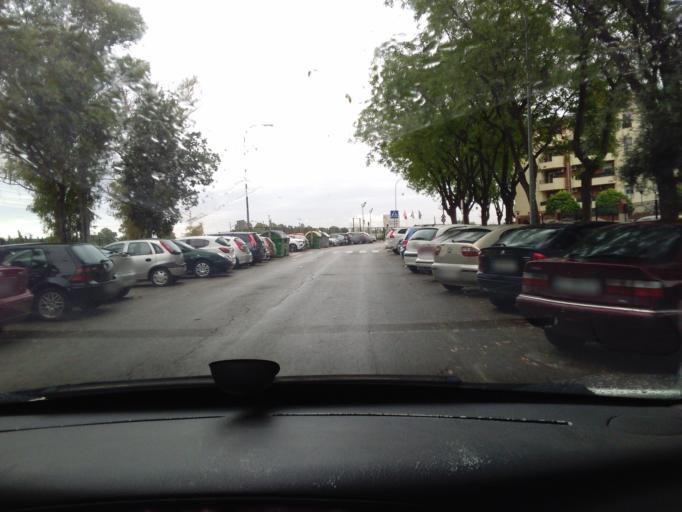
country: ES
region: Andalusia
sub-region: Provincia de Sevilla
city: Sevilla
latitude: 37.4021
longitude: -5.9364
